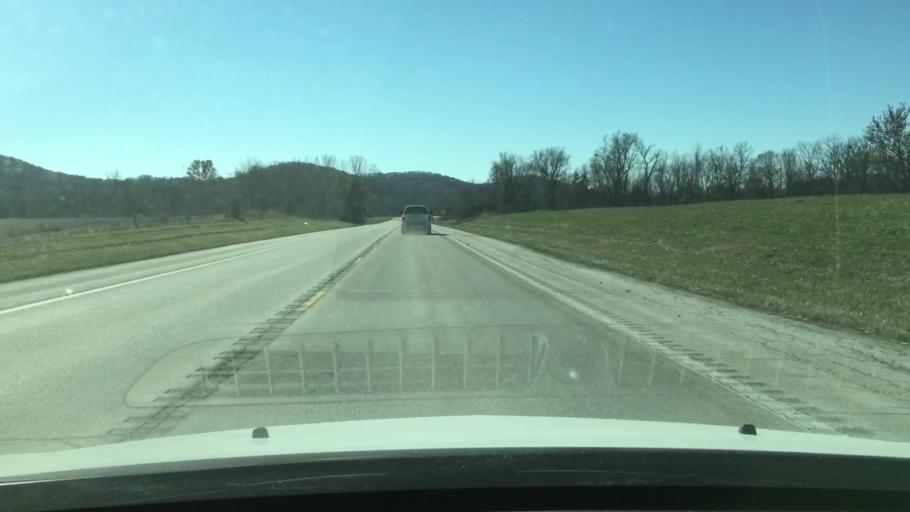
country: US
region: Missouri
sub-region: Pike County
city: Louisiana
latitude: 39.4254
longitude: -91.0847
